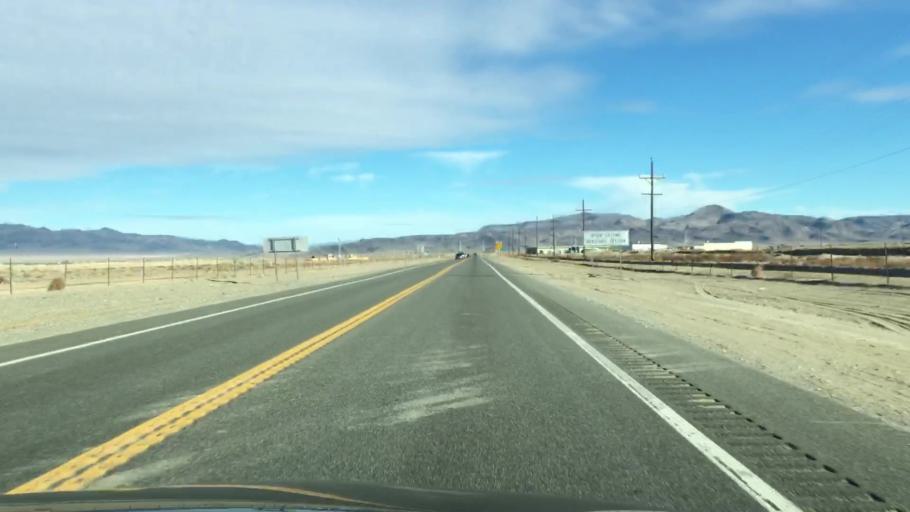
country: US
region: Nevada
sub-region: Mineral County
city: Hawthorne
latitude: 38.5245
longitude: -118.6036
